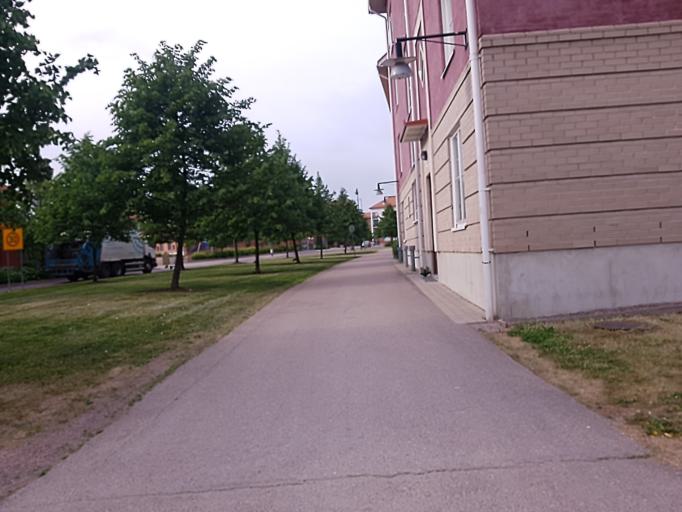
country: FI
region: Uusimaa
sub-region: Helsinki
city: Vantaa
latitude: 60.2835
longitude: 24.9591
